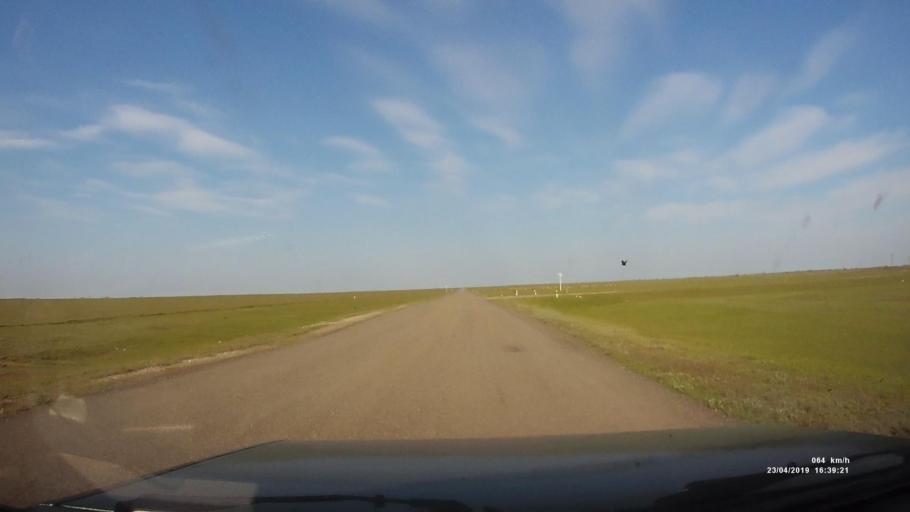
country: RU
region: Kalmykiya
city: Priyutnoye
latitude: 46.3392
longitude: 43.1646
